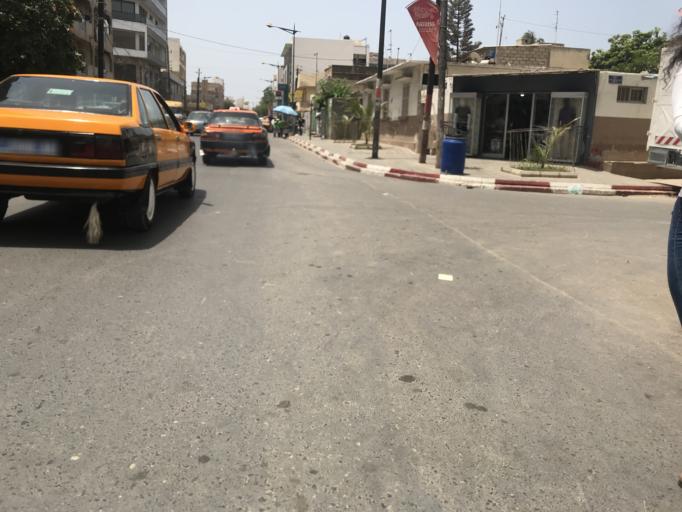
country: SN
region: Dakar
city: Dakar
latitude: 14.6783
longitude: -17.4533
